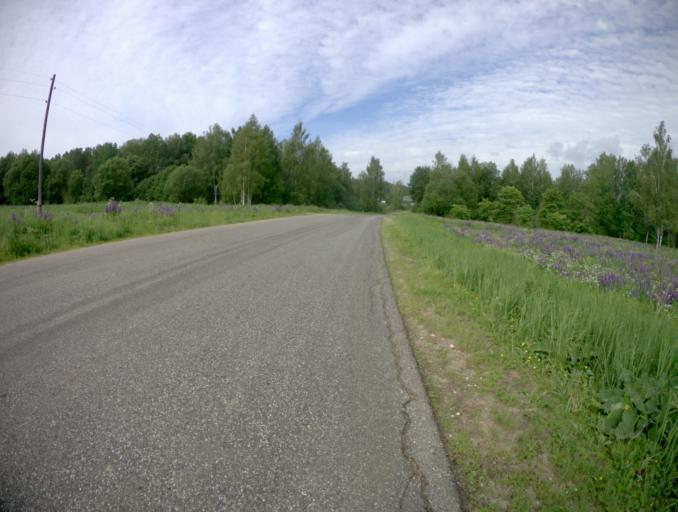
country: RU
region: Vladimir
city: Lakinsk
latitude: 56.0661
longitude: 39.9174
